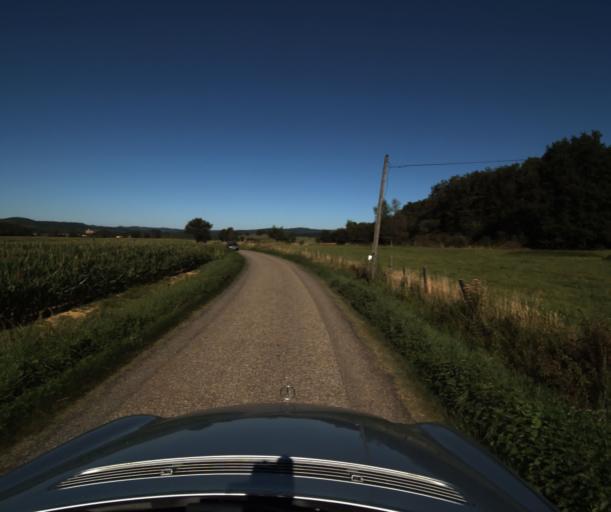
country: FR
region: Midi-Pyrenees
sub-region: Departement de l'Ariege
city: Lavelanet
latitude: 42.9803
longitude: 1.8938
